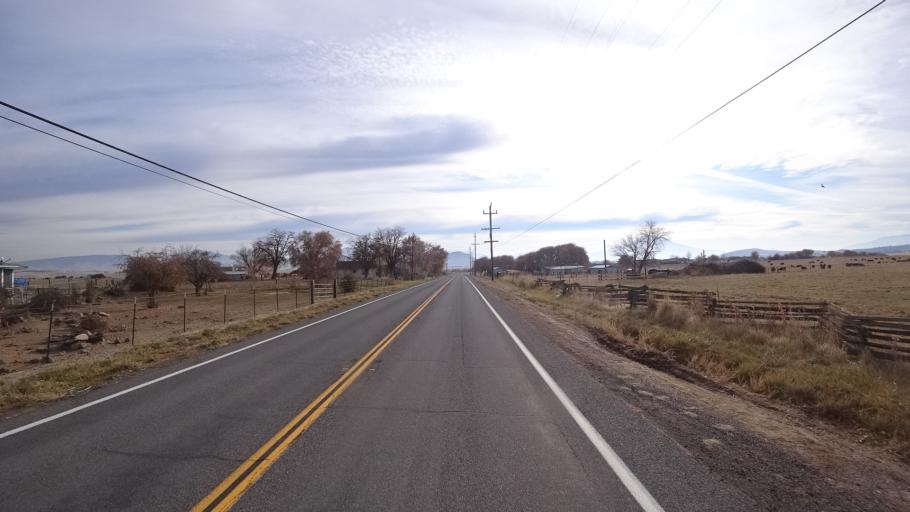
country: US
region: California
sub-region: Siskiyou County
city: Montague
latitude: 41.7302
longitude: -122.5760
